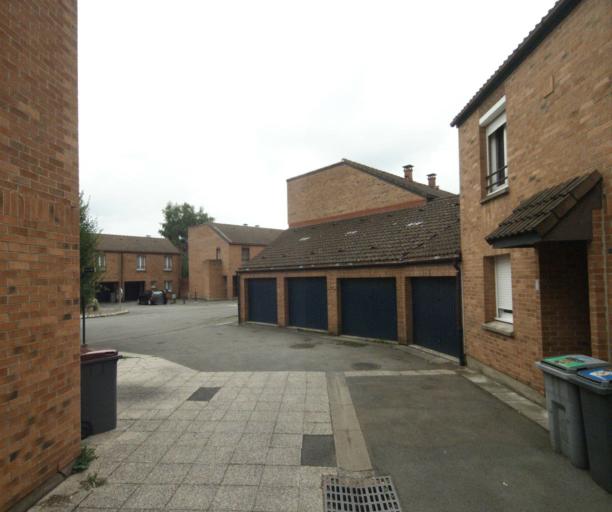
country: FR
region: Nord-Pas-de-Calais
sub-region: Departement du Nord
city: Wasquehal
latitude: 50.6474
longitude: 3.1352
